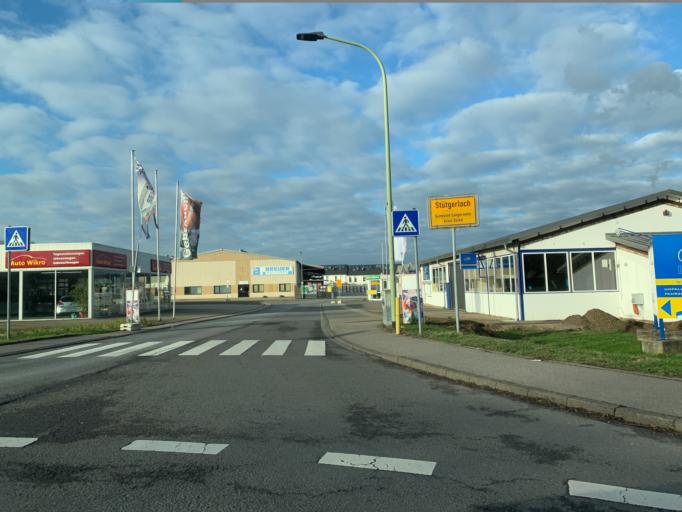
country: DE
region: North Rhine-Westphalia
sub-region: Regierungsbezirk Koln
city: Langerwehe
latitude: 50.8149
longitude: 6.3748
